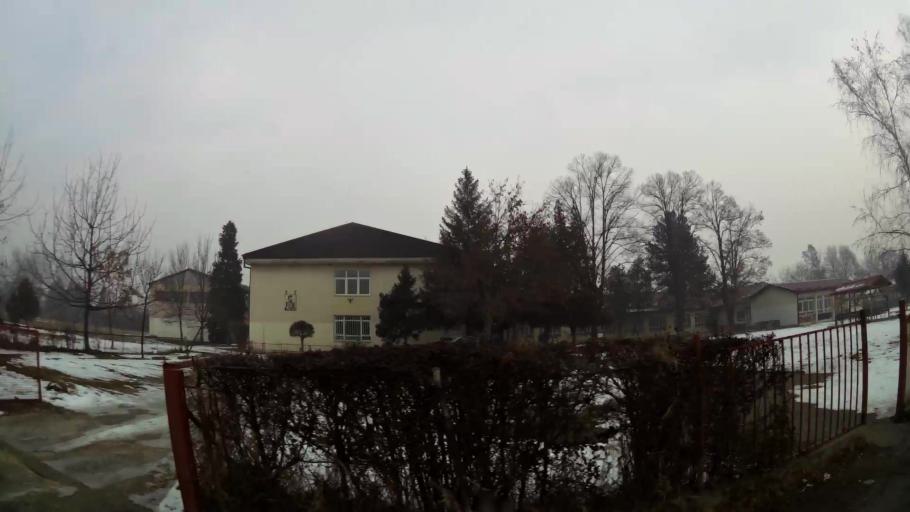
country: MK
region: Ilinden
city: Jurumleri
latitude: 41.9633
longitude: 21.5613
